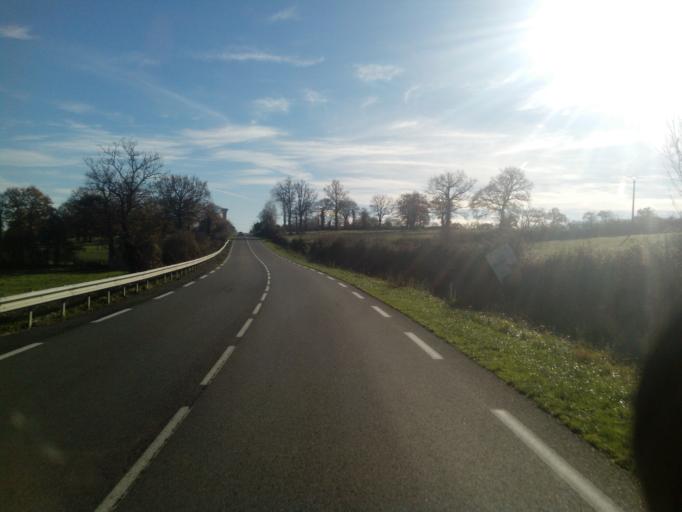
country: FR
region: Limousin
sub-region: Departement de la Haute-Vienne
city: Peyrat-de-Bellac
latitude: 46.1549
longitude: 0.9615
